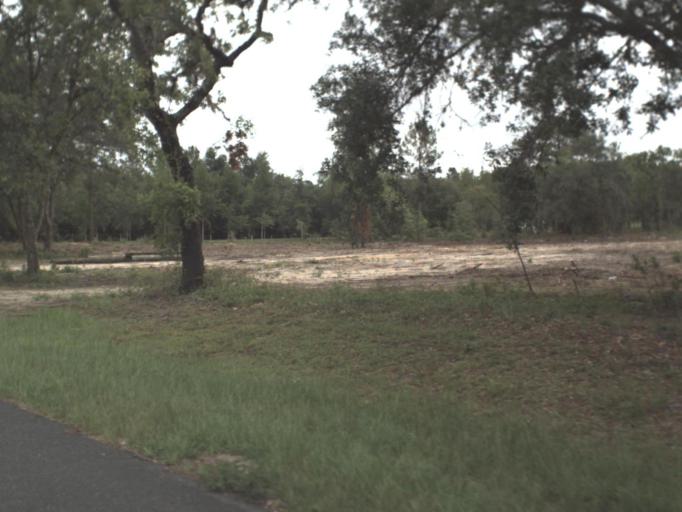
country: US
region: Florida
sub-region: Levy County
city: Williston Highlands
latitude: 29.2353
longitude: -82.4412
